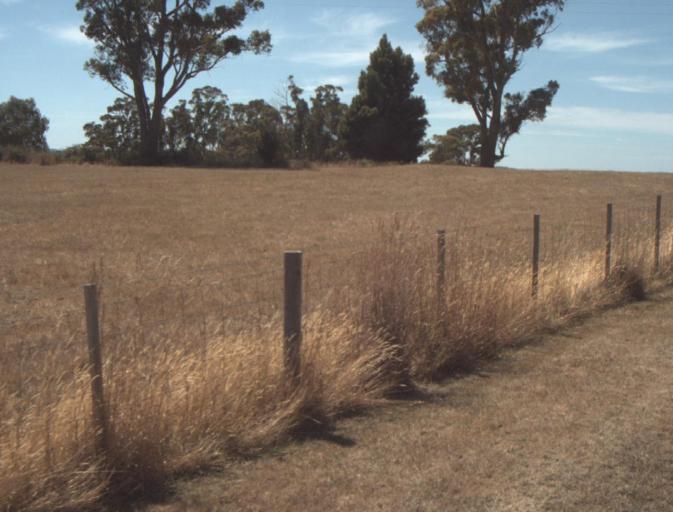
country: AU
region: Tasmania
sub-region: Launceston
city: Mayfield
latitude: -41.2433
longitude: 147.1292
